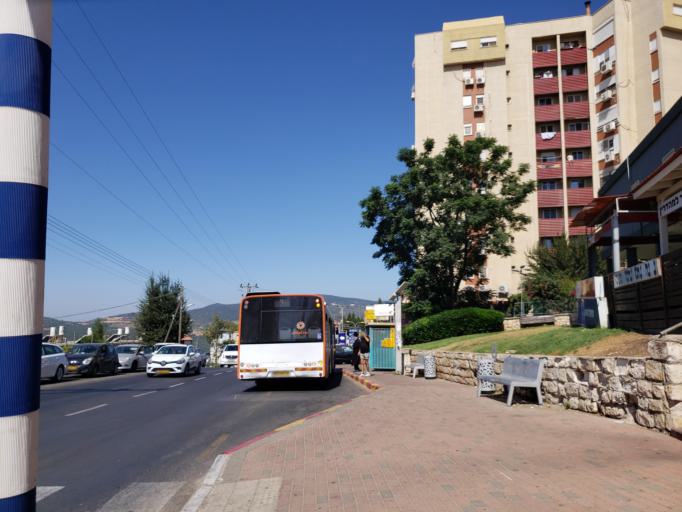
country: IL
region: Northern District
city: Safed
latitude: 32.9574
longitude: 35.4965
